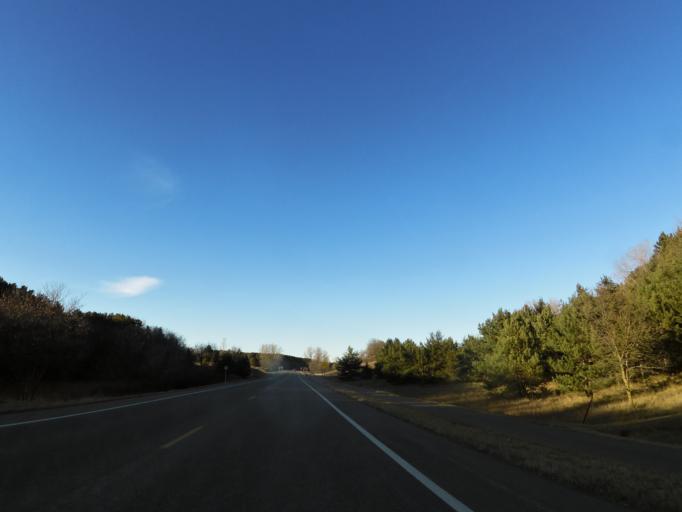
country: US
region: Minnesota
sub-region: Washington County
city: Stillwater
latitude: 45.1191
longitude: -92.8351
